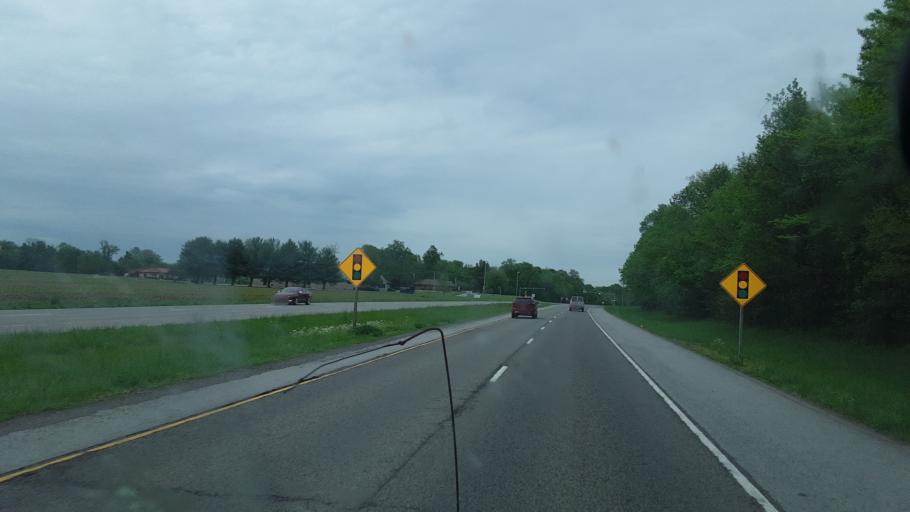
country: US
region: Illinois
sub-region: Jackson County
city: Murphysboro
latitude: 37.7659
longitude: -89.3012
